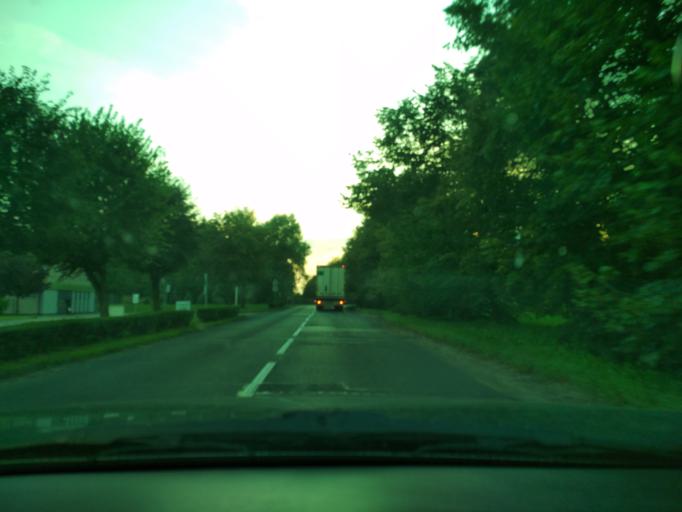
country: PL
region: Silesian Voivodeship
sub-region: Gliwice
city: Gliwice
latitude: 50.2666
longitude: 18.7038
